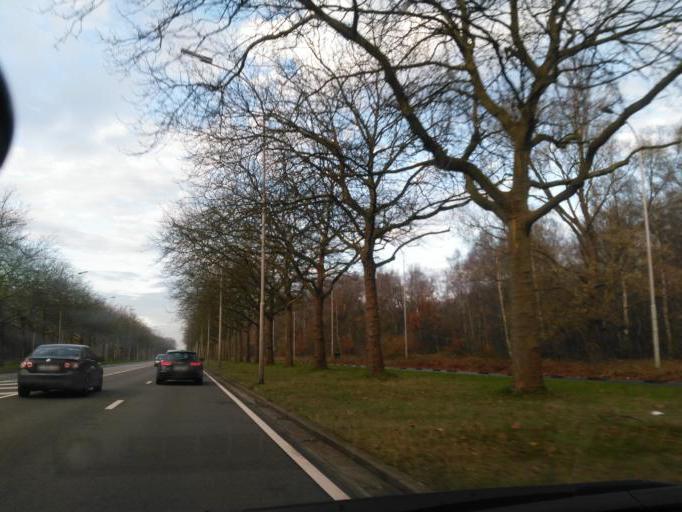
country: BE
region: Flanders
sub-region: Provincie Antwerpen
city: Antwerpen
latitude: 51.2276
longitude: 4.3707
